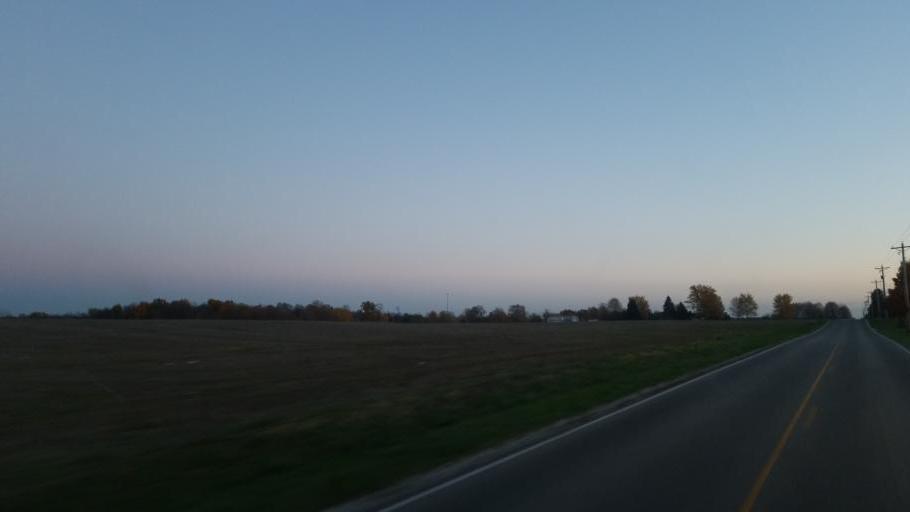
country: US
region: Ohio
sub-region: Huron County
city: Plymouth
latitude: 40.9557
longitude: -82.7433
